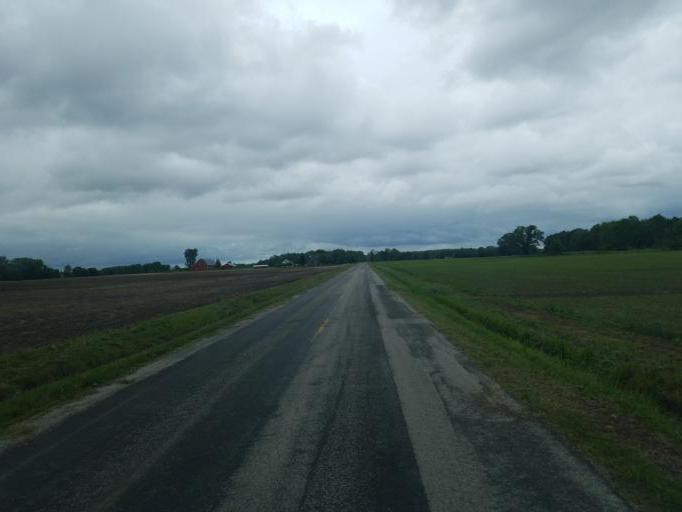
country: US
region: Ohio
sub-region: Morrow County
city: Cardington
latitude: 40.5385
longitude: -82.9768
